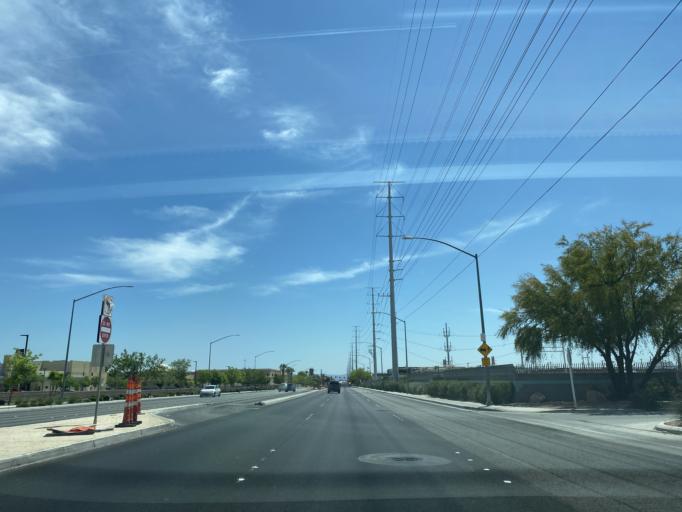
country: US
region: Nevada
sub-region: Clark County
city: North Las Vegas
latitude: 36.2456
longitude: -115.1169
